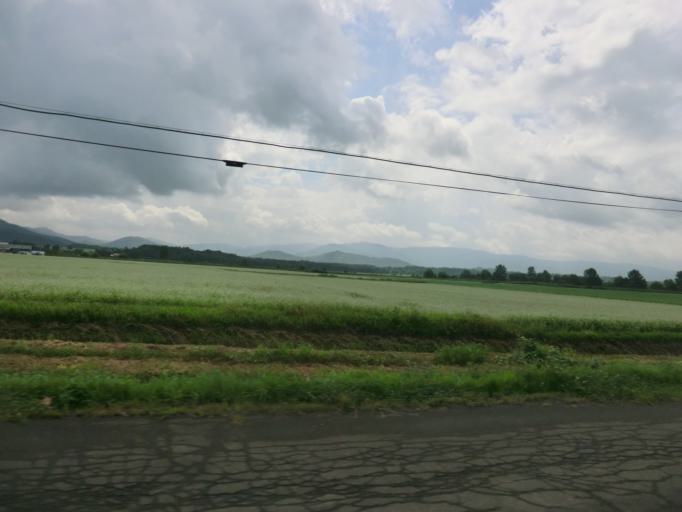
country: JP
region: Hokkaido
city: Fukagawa
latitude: 44.0042
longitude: 142.1475
